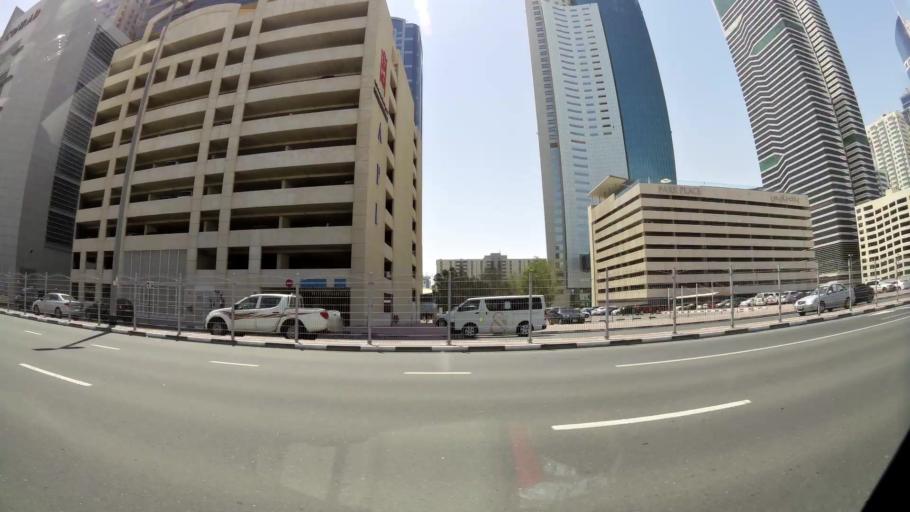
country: AE
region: Ash Shariqah
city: Sharjah
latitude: 25.2259
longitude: 55.2821
